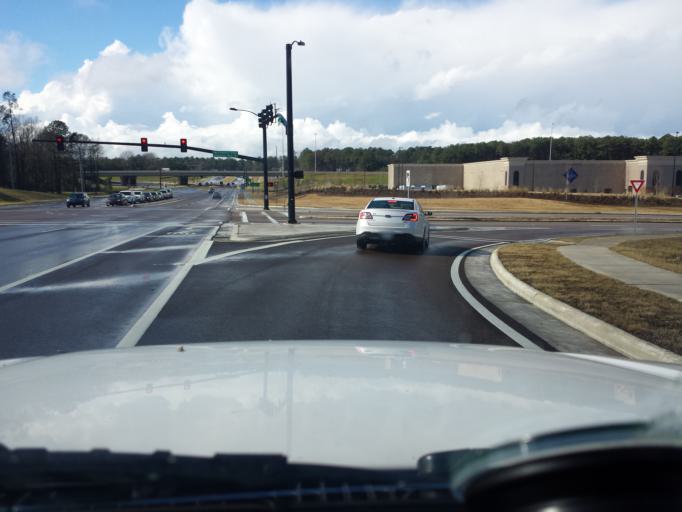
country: US
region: Mississippi
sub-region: Madison County
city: Madison
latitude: 32.4580
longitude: -90.1381
